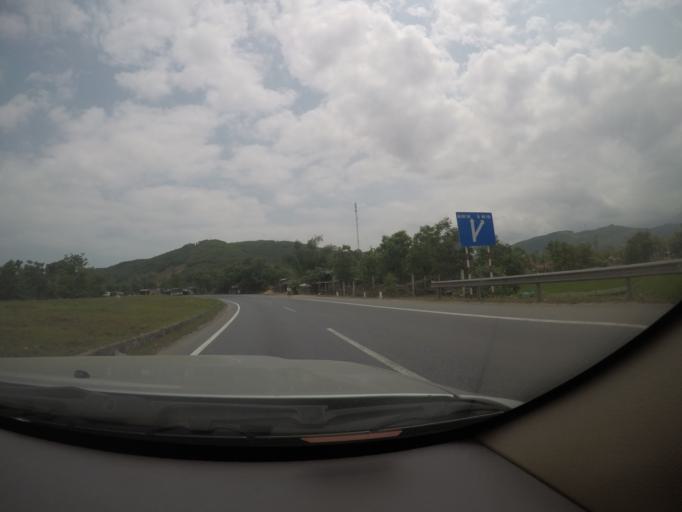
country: VN
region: Thua Thien-Hue
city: Phu Loc
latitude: 16.2692
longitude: 107.8965
